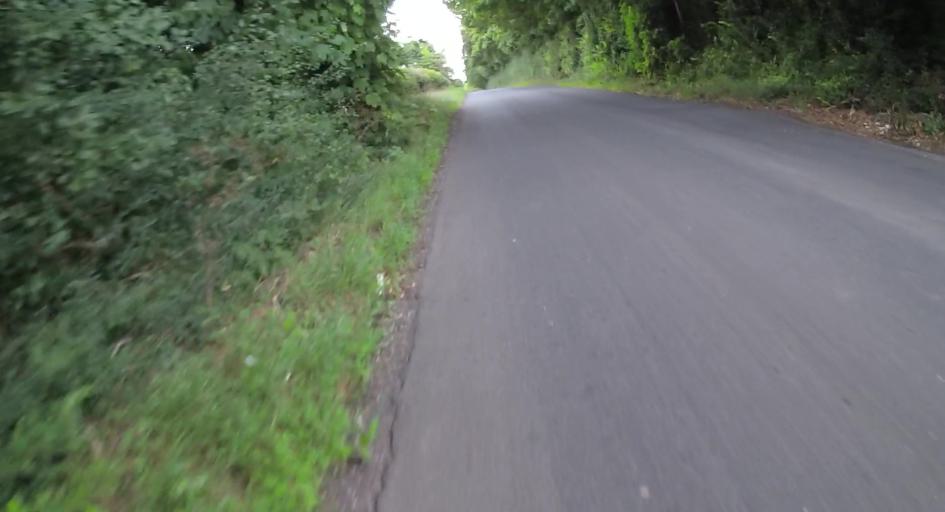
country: GB
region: England
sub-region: Hampshire
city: Kings Worthy
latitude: 51.1316
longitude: -1.3094
